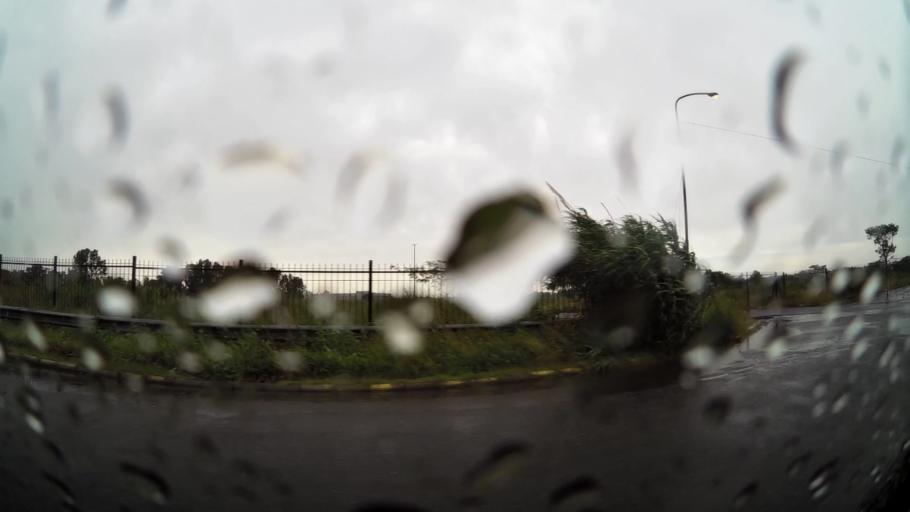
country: AR
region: Buenos Aires F.D.
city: Villa Lugano
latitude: -34.6664
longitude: -58.4557
